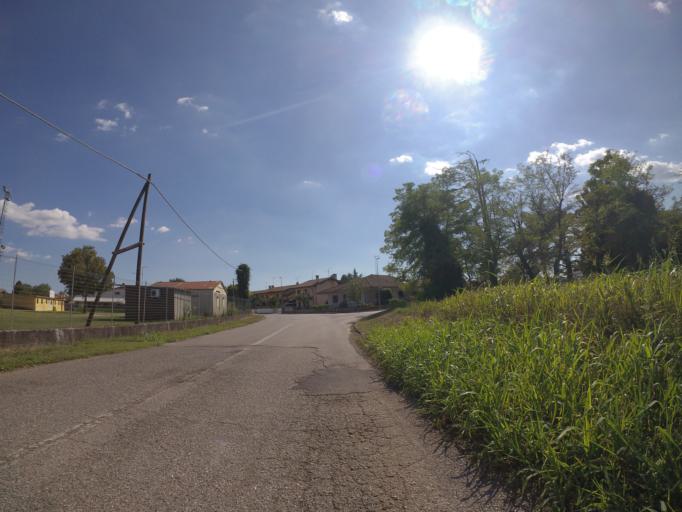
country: IT
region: Friuli Venezia Giulia
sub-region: Provincia di Udine
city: Talmassons
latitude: 45.9245
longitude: 13.1399
